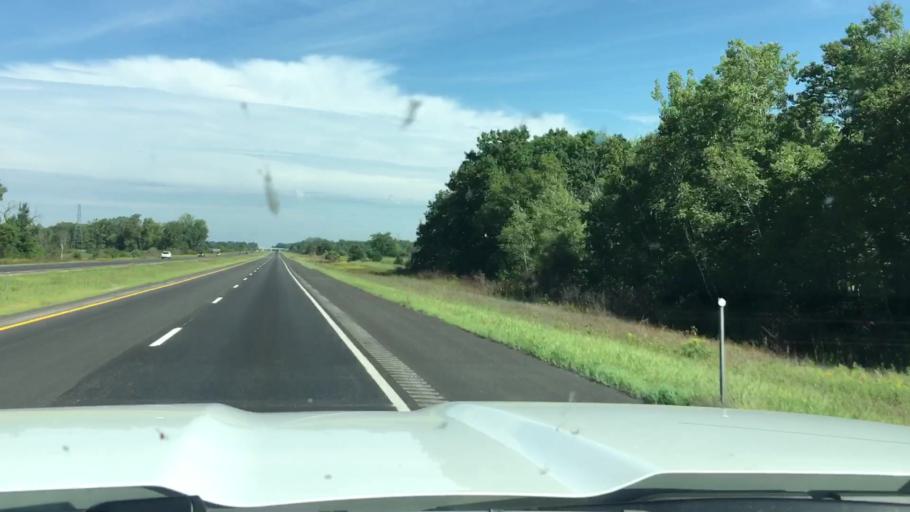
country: US
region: Michigan
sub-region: Saginaw County
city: Freeland
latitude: 43.5490
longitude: -84.1387
